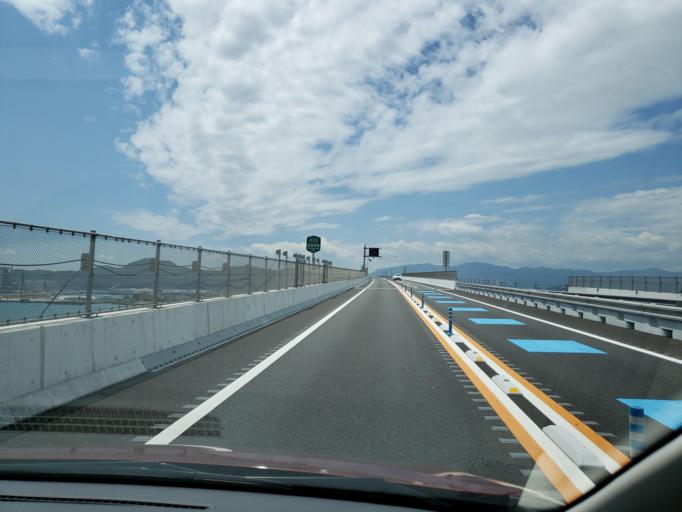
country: JP
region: Tokushima
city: Tokushima-shi
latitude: 34.0574
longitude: 134.5895
